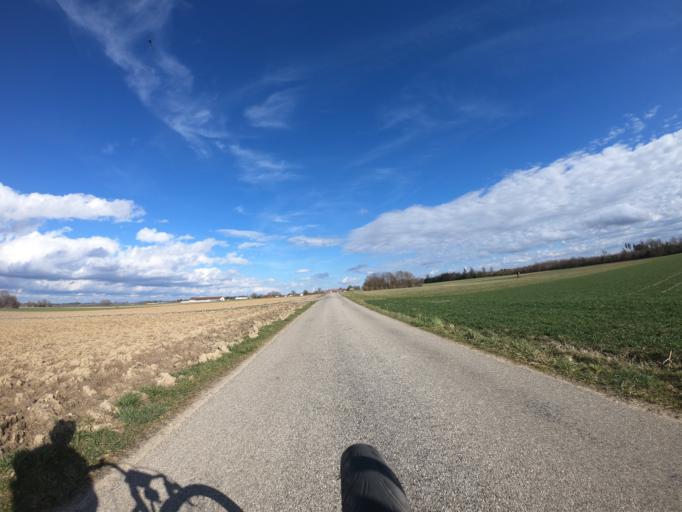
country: DE
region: Bavaria
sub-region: Upper Bavaria
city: Landsberied
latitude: 48.1846
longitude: 11.2047
